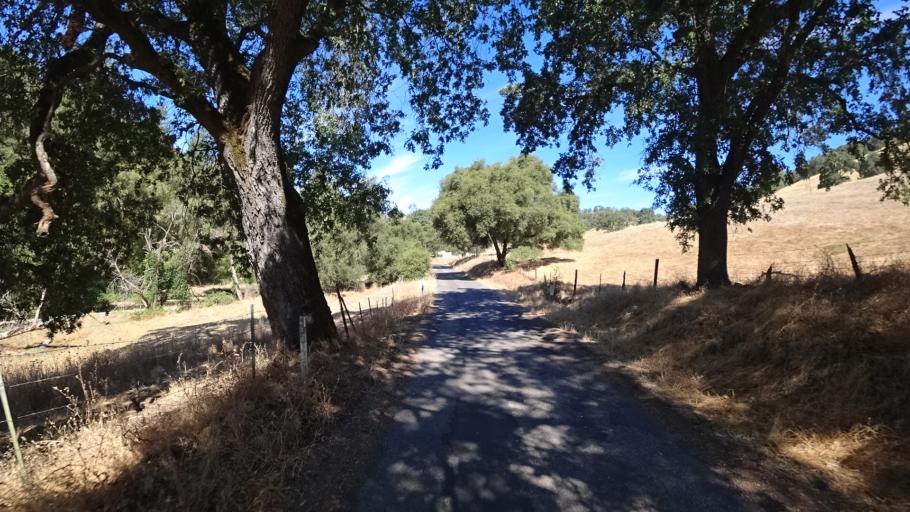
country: US
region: California
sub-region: Calaveras County
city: Angels Camp
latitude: 38.1473
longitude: -120.5818
